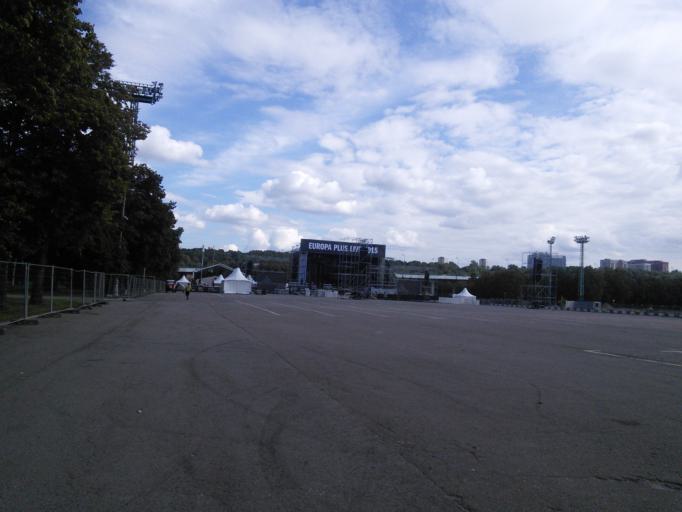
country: RU
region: Moscow
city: Luzhniki
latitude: 55.7163
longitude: 37.5614
